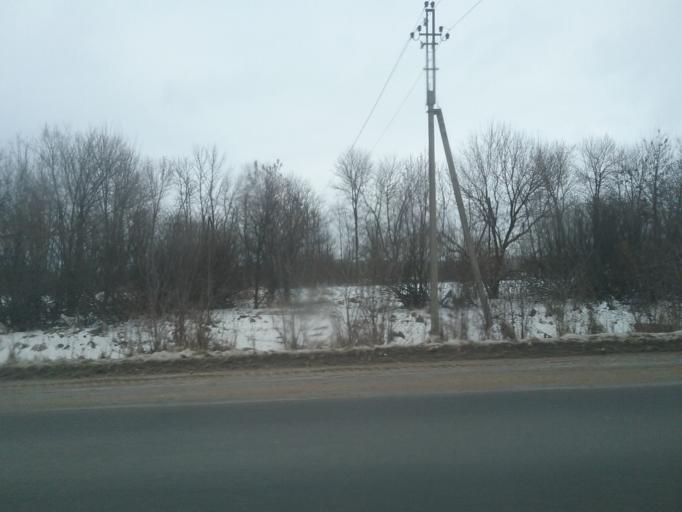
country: RU
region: Tula
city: Bolokhovo
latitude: 54.0645
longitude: 37.7999
